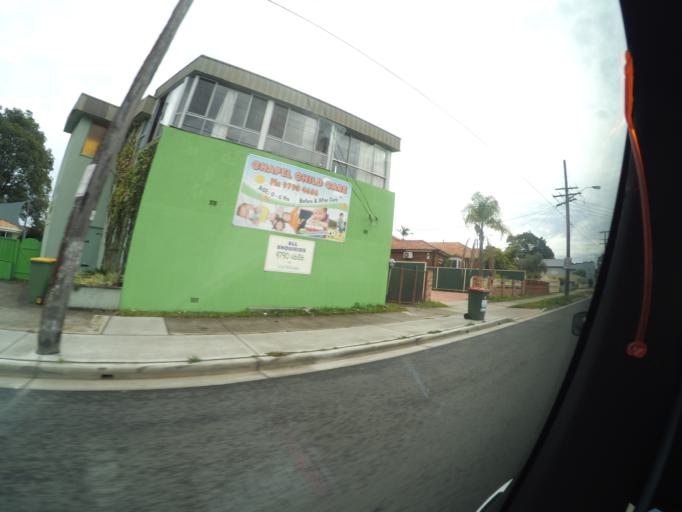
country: AU
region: New South Wales
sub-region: Bankstown
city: Bankstown
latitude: -33.9321
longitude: 151.0281
